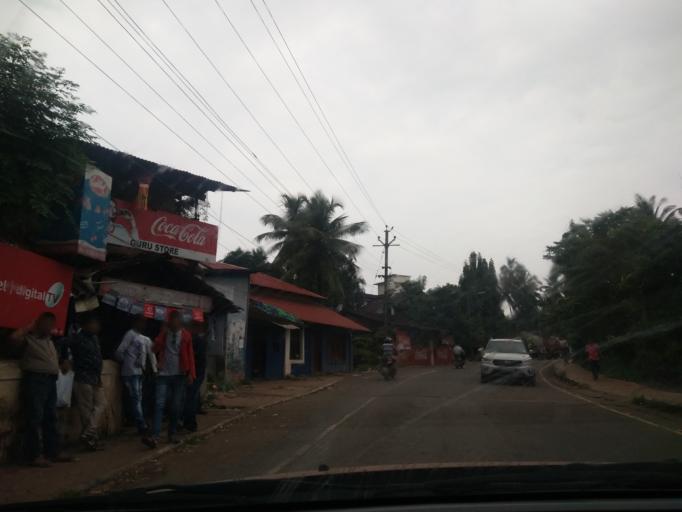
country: IN
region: Goa
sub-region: South Goa
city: Sancoale
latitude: 15.3568
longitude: 73.9275
